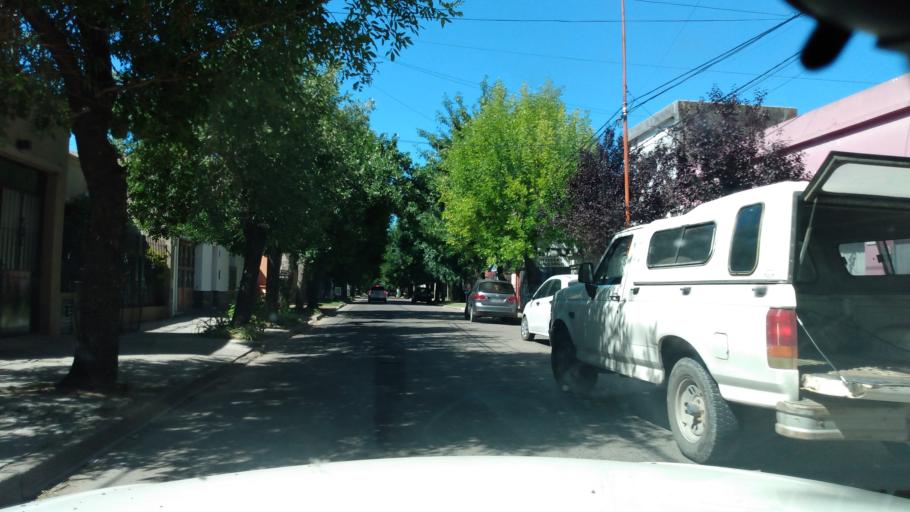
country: AR
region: Buenos Aires
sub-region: Partido de Lujan
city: Lujan
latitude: -34.5656
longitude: -59.1085
